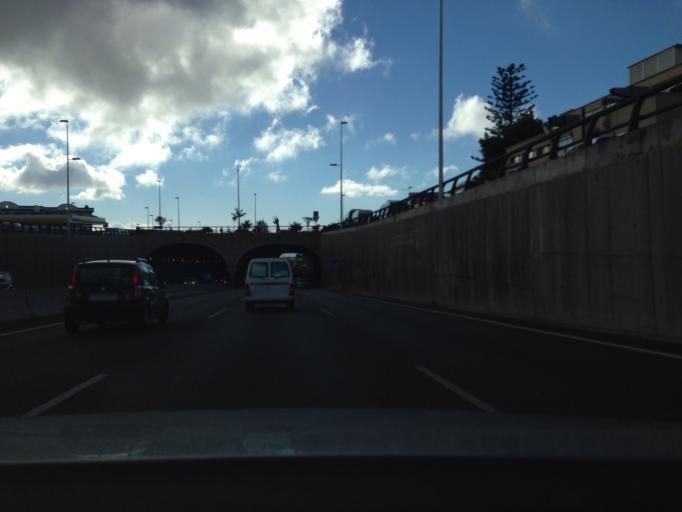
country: ES
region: Canary Islands
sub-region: Provincia de Santa Cruz de Tenerife
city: La Laguna
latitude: 28.4820
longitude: -16.3195
